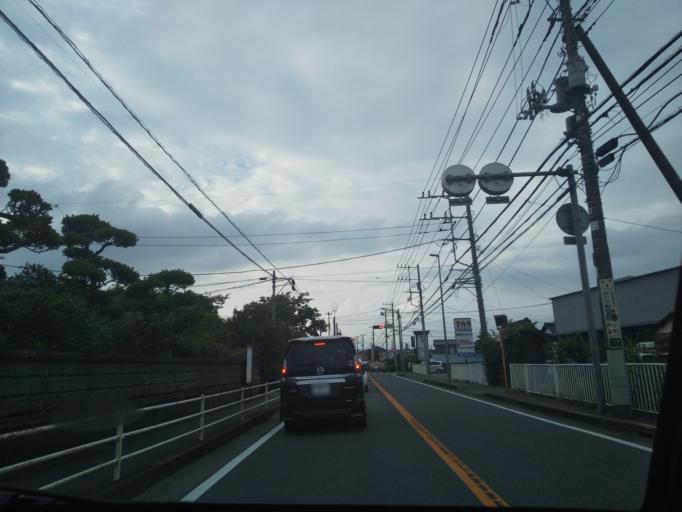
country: JP
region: Kanagawa
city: Zama
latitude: 35.4688
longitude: 139.3887
